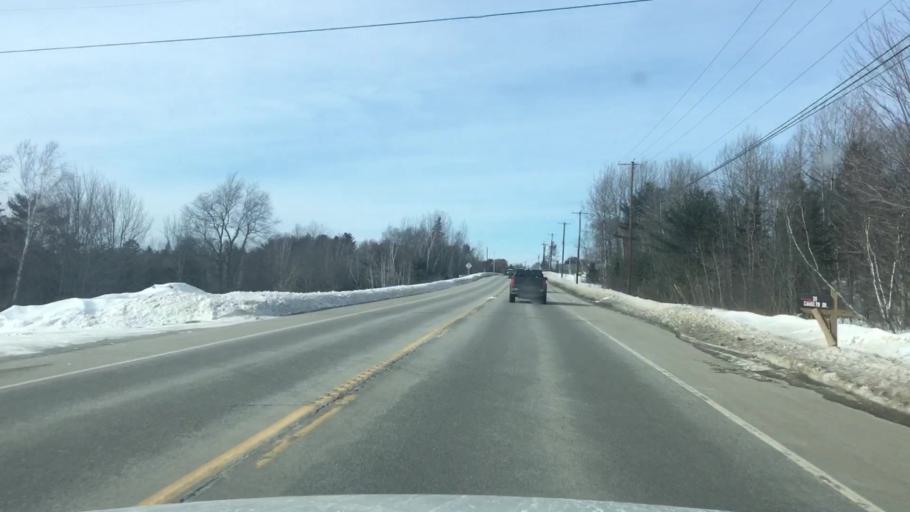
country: US
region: Maine
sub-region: Penobscot County
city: Kenduskeag
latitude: 44.9296
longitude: -68.9356
